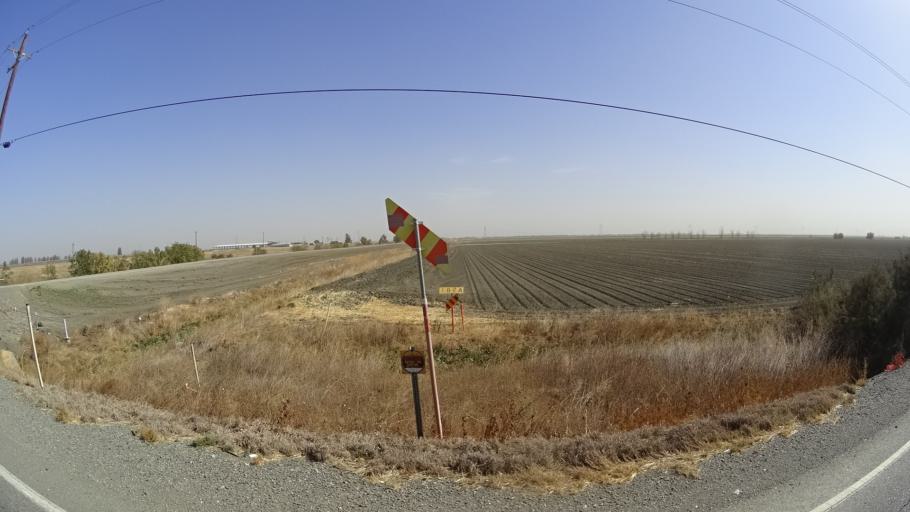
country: US
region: California
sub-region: Yolo County
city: Davis
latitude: 38.5891
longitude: -121.6748
